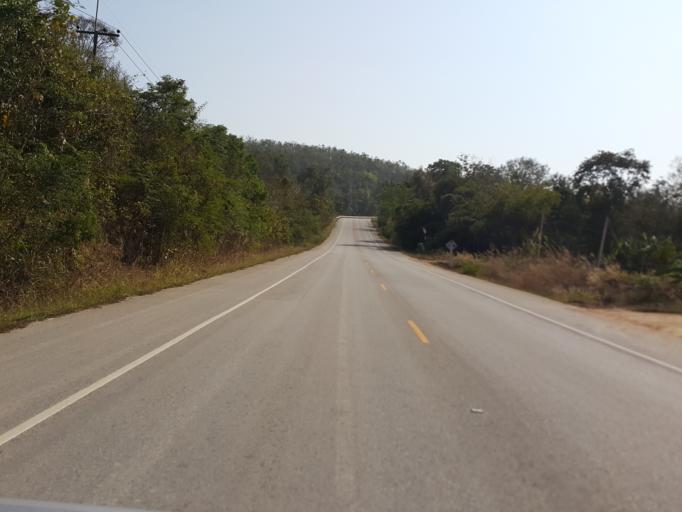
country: TH
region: Lampang
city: Chae Hom
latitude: 18.7838
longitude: 99.5845
